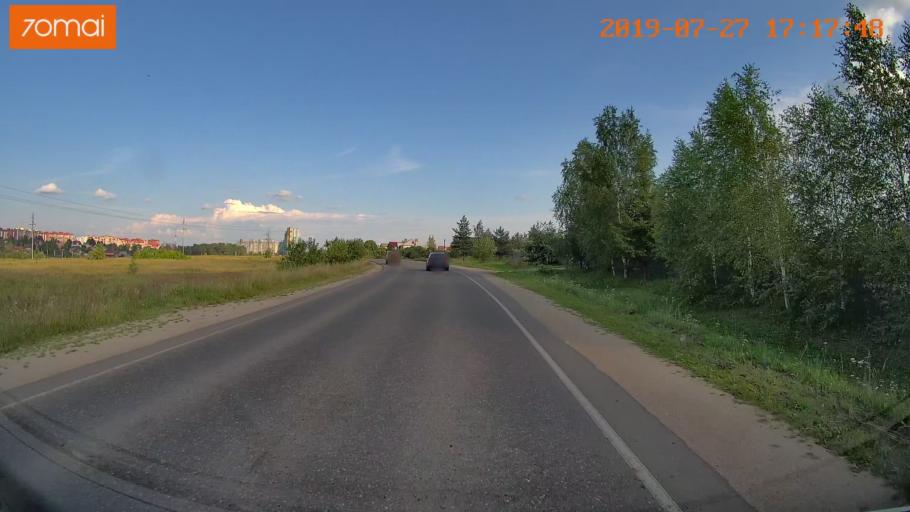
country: RU
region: Ivanovo
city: Novo-Talitsy
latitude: 57.0343
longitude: 40.8986
